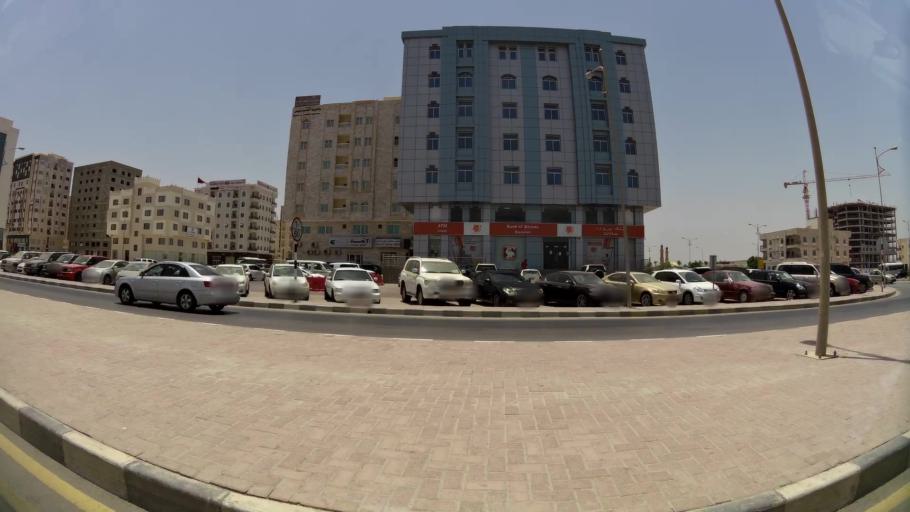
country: OM
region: Zufar
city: Salalah
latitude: 17.0197
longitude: 54.1000
